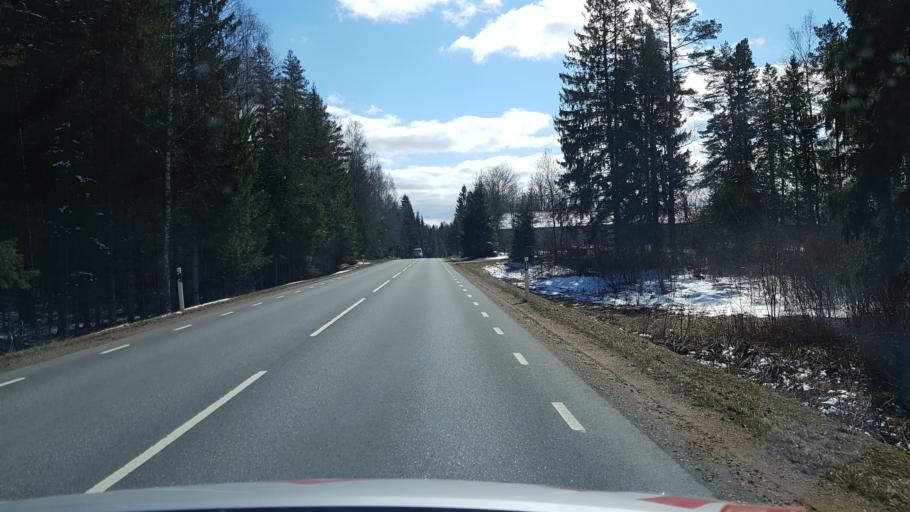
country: EE
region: Laeaene-Virumaa
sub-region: Kadrina vald
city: Kadrina
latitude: 59.3921
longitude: 26.0145
